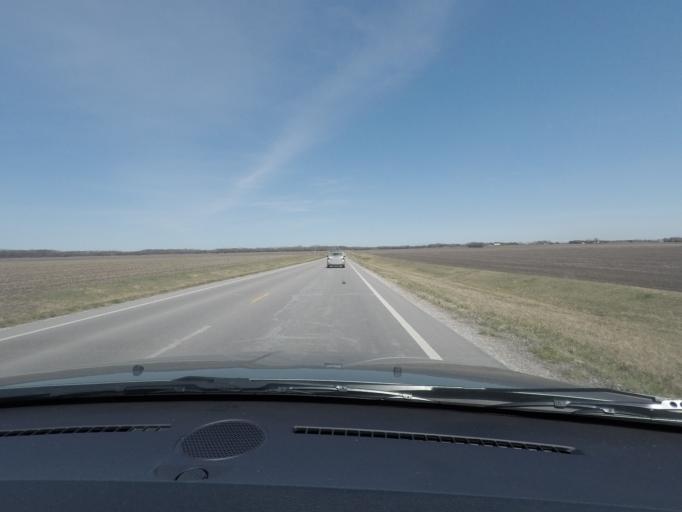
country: US
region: Kansas
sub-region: Lyon County
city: Emporia
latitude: 38.4381
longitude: -96.1705
